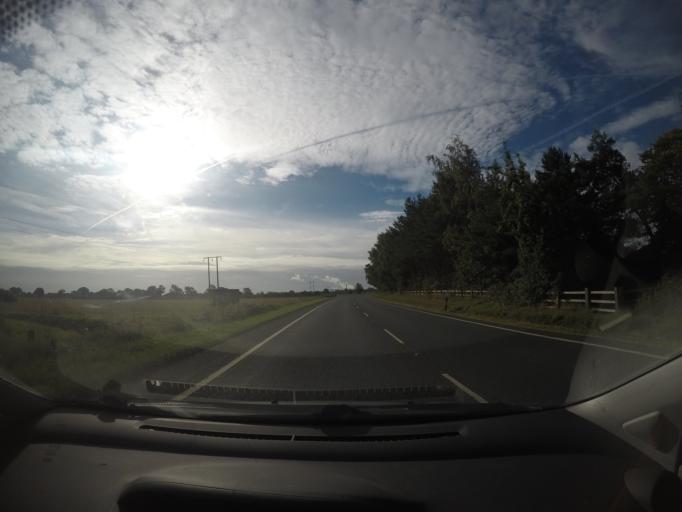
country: GB
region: England
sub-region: North Yorkshire
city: Barlby
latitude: 53.8074
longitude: -1.0372
